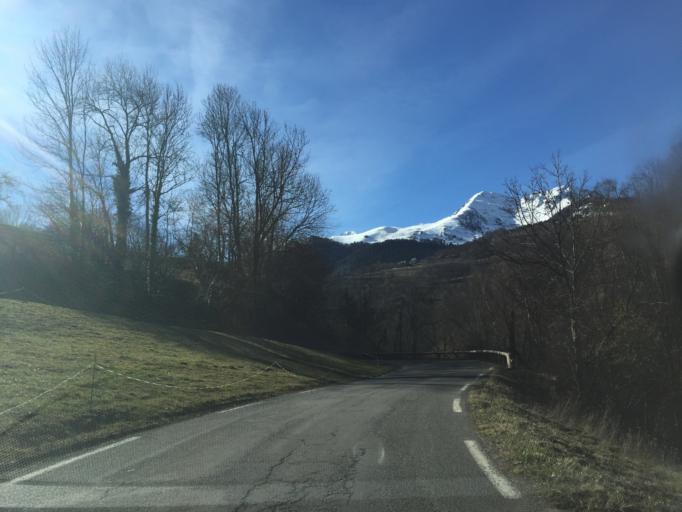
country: FR
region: Midi-Pyrenees
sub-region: Departement des Hautes-Pyrenees
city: Saint-Lary-Soulan
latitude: 42.8168
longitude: 0.3439
